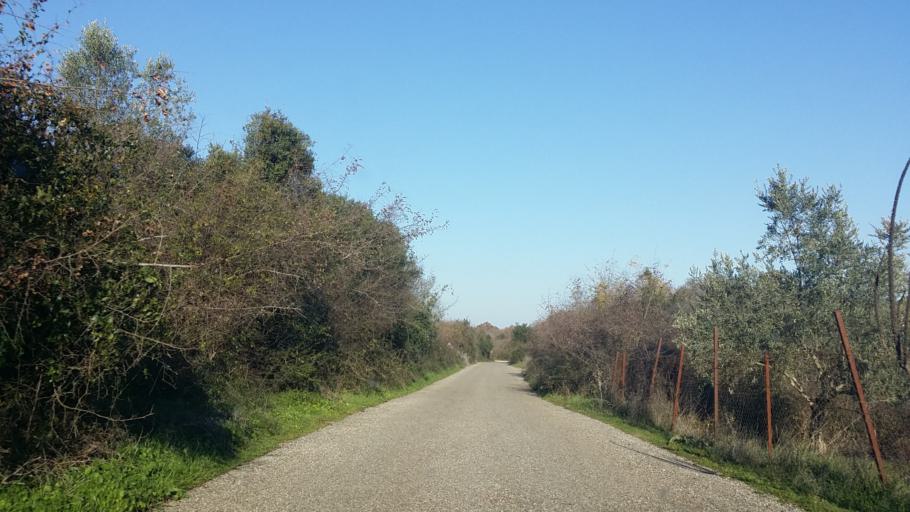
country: GR
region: West Greece
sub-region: Nomos Aitolias kai Akarnanias
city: Katouna
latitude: 38.7585
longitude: 21.1434
